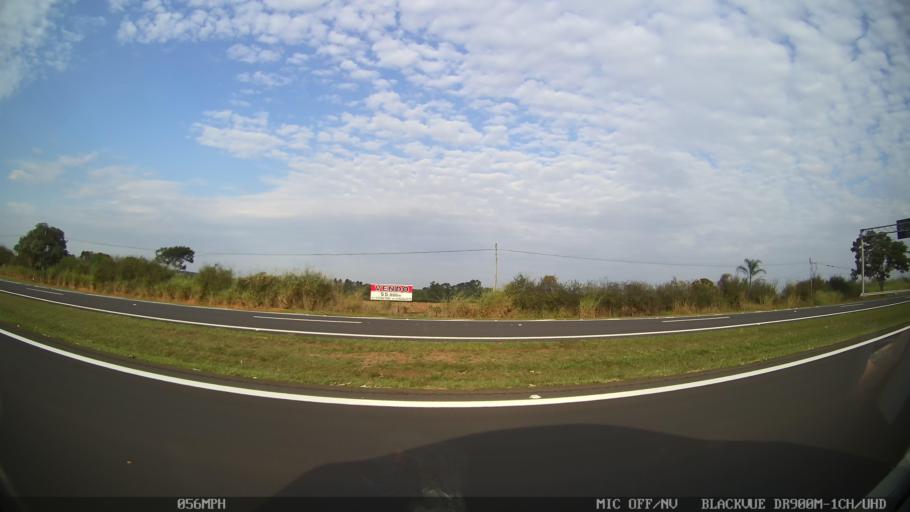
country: BR
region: Sao Paulo
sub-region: Artur Nogueira
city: Artur Nogueira
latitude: -22.5980
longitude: -47.1882
